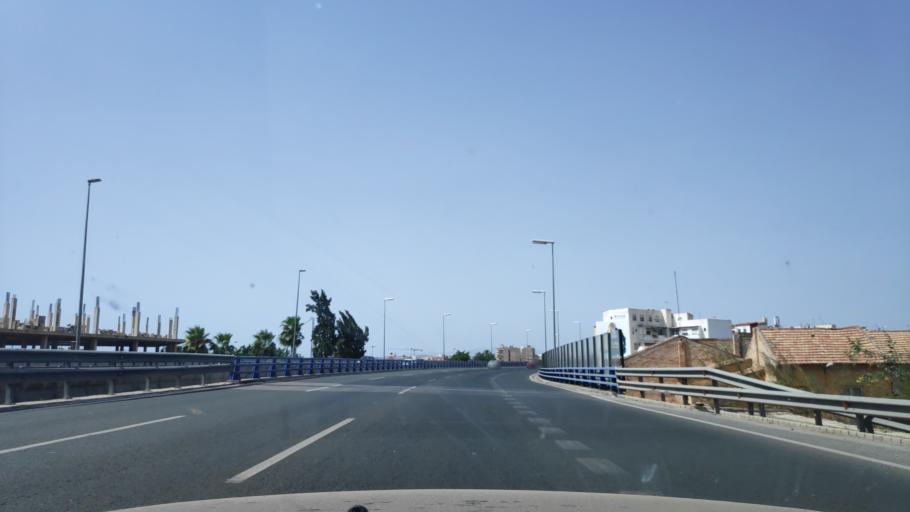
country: ES
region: Murcia
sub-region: Murcia
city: Murcia
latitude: 37.9687
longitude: -1.1378
